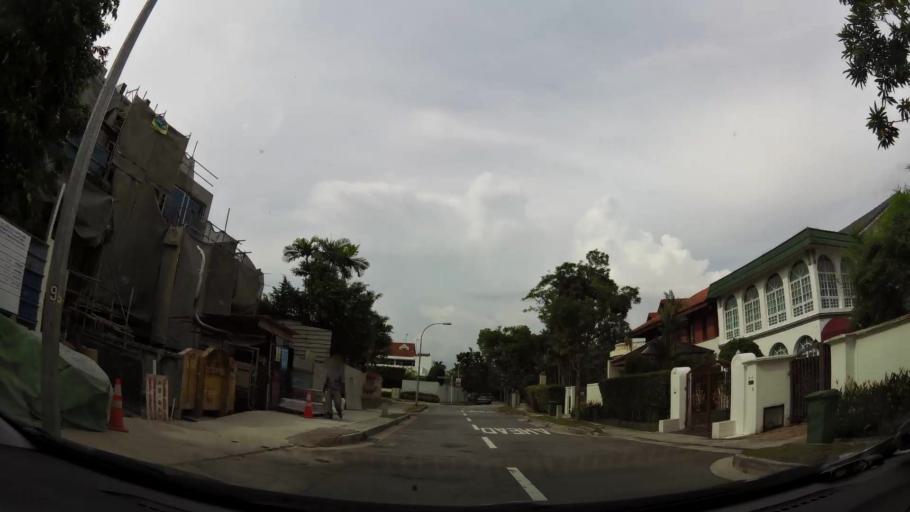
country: SG
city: Singapore
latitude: 1.3373
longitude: 103.7861
